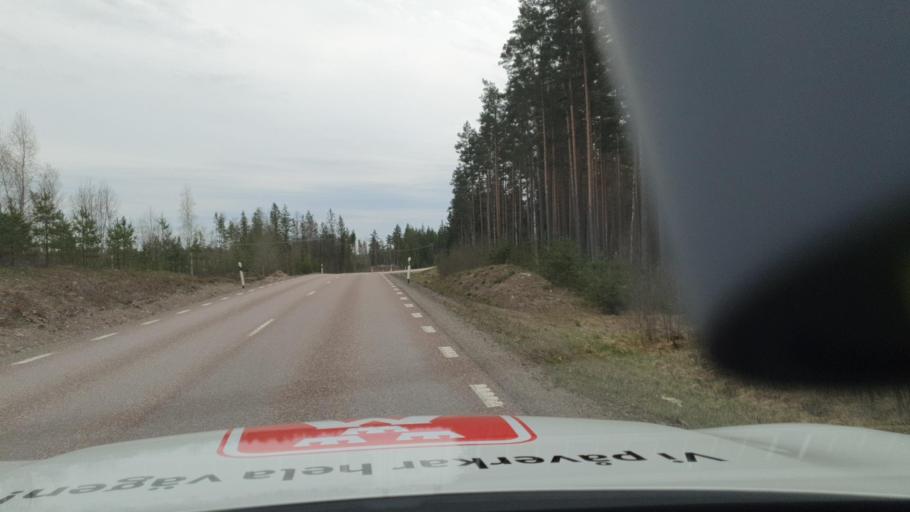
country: SE
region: Gaevleborg
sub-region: Gavle Kommun
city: Gavle
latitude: 60.5853
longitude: 17.1301
